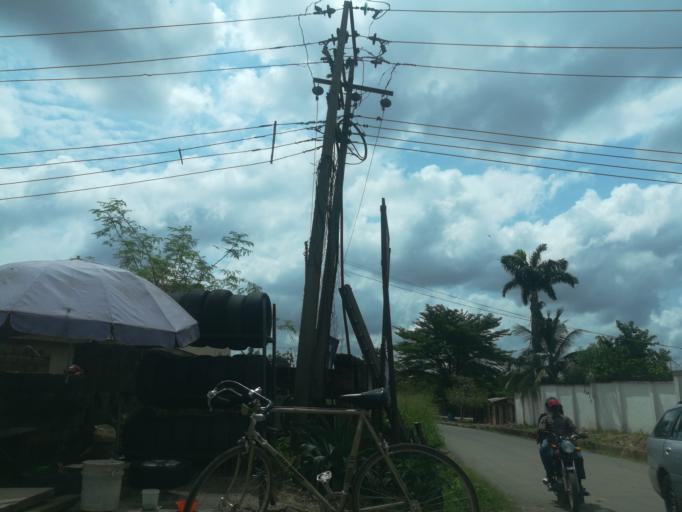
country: NG
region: Oyo
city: Ibadan
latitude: 7.3658
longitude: 3.8377
